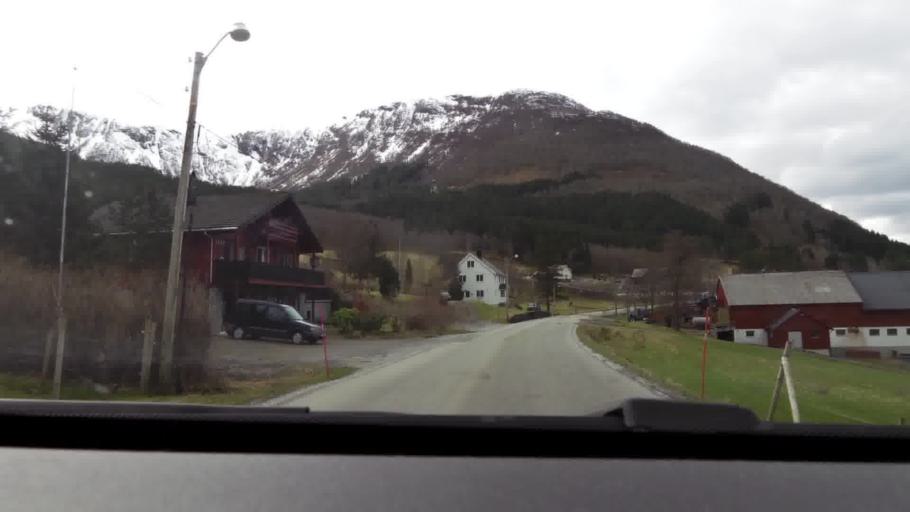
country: NO
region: More og Romsdal
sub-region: Kristiansund
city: Kristiansund
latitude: 63.1143
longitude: 7.7641
